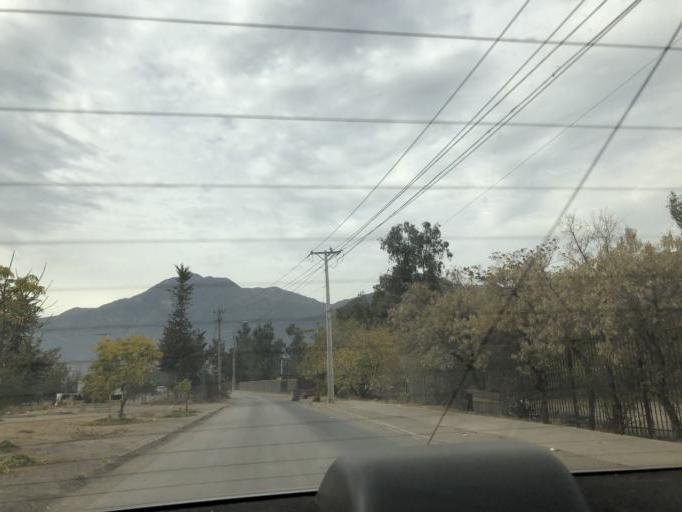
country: CL
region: Santiago Metropolitan
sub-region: Provincia de Cordillera
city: Puente Alto
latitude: -33.6063
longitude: -70.5159
